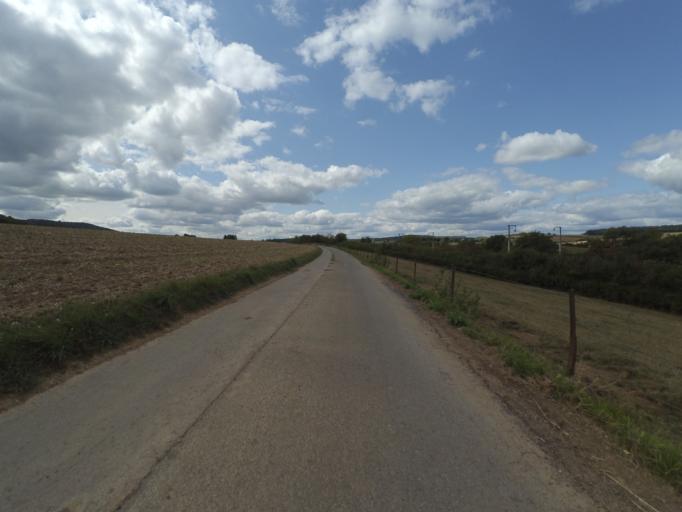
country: LU
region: Grevenmacher
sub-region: Canton de Grevenmacher
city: Betzdorf
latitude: 49.6831
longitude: 6.3266
